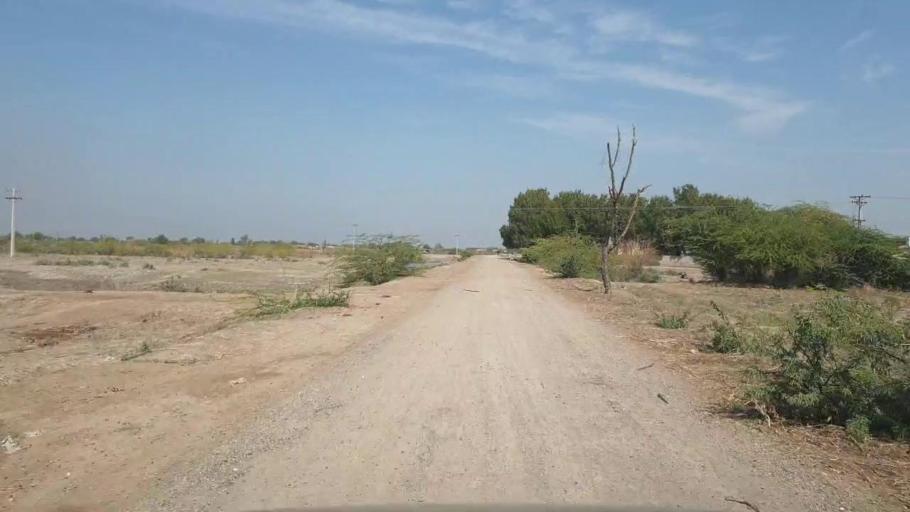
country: PK
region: Sindh
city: Mirwah Gorchani
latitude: 25.4391
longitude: 69.1893
